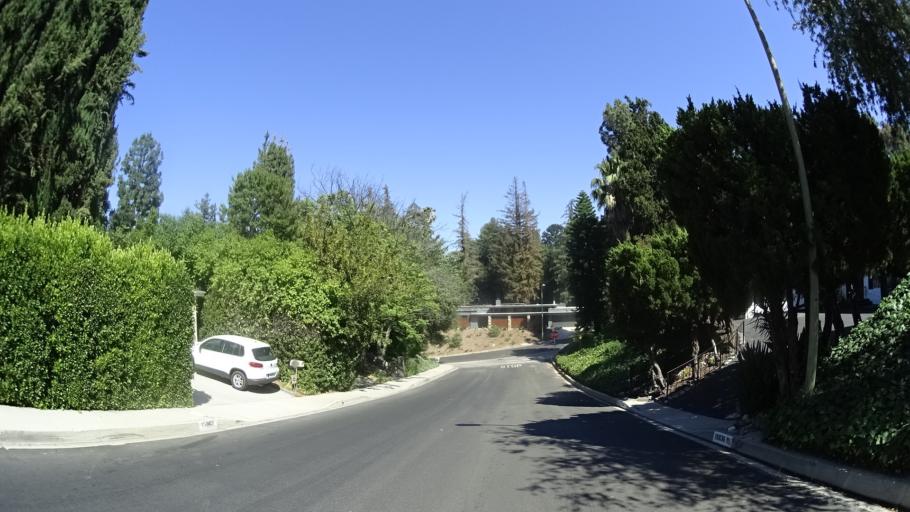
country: US
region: California
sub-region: Los Angeles County
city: Sherman Oaks
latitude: 34.1352
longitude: -118.4787
